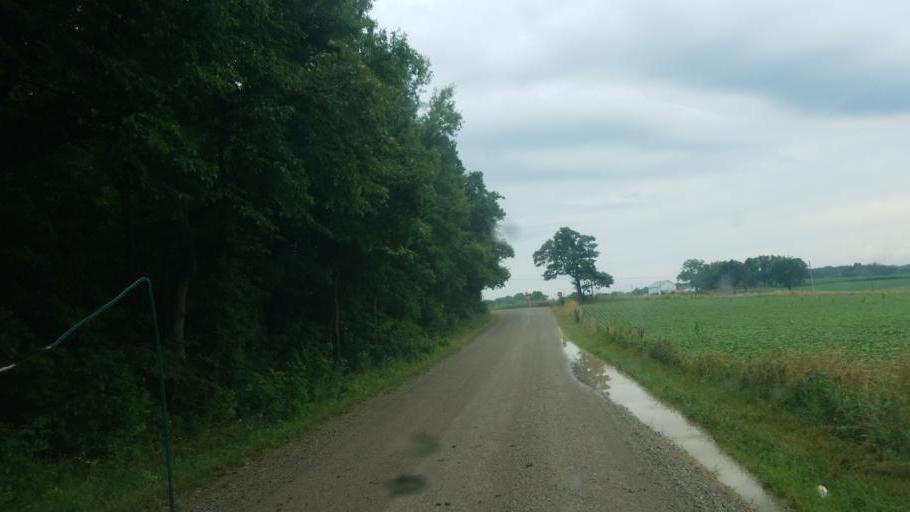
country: US
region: Indiana
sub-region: Steuben County
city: Hamilton
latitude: 41.5157
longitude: -84.9330
